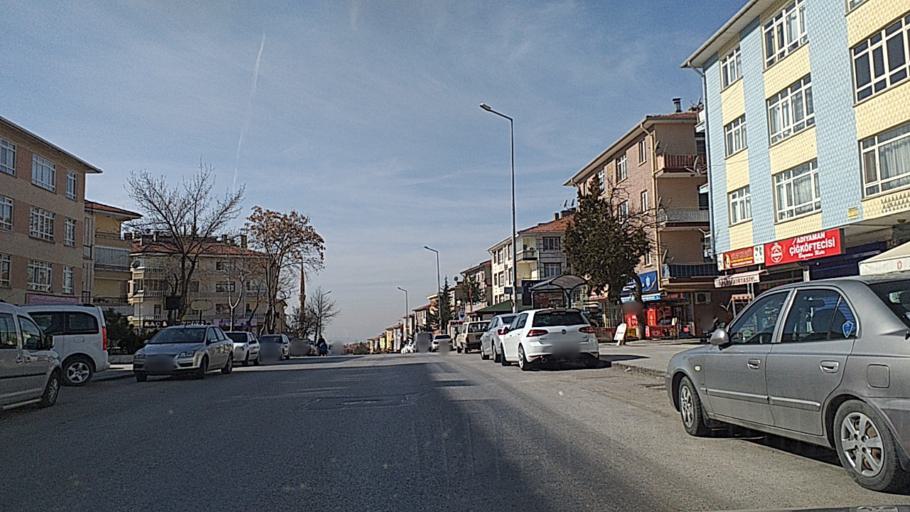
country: TR
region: Ankara
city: Ankara
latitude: 39.9822
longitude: 32.8302
